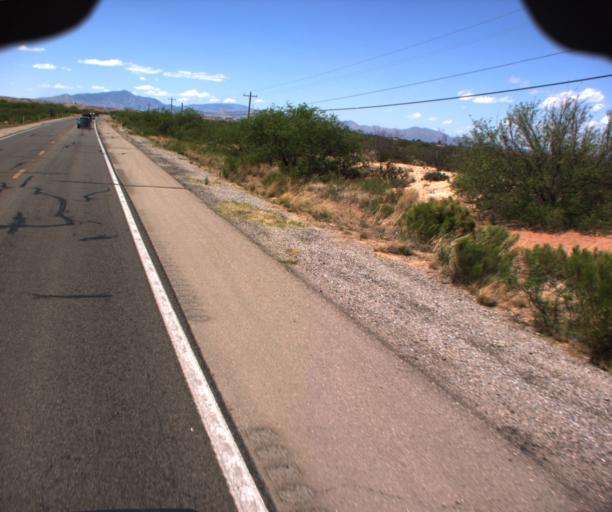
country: US
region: Arizona
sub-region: Cochise County
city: Benson
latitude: 31.9256
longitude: -110.2748
